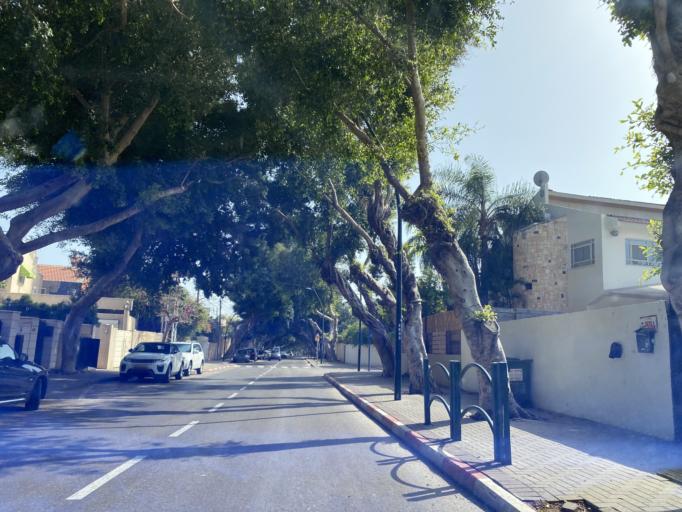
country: IL
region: Tel Aviv
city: Herzliya Pituah
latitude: 32.1728
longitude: 34.8079
